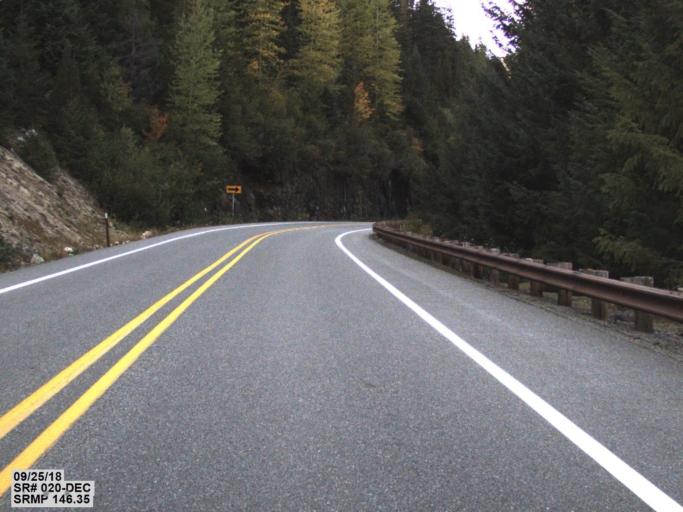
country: US
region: Washington
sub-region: Snohomish County
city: Darrington
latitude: 48.6486
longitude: -120.8575
